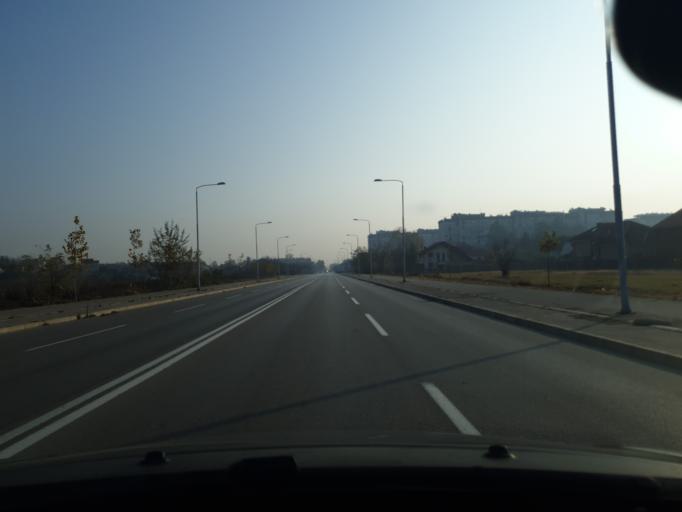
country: RS
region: Central Serbia
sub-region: Jablanicki Okrug
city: Leskovac
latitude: 43.0036
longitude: 21.9291
